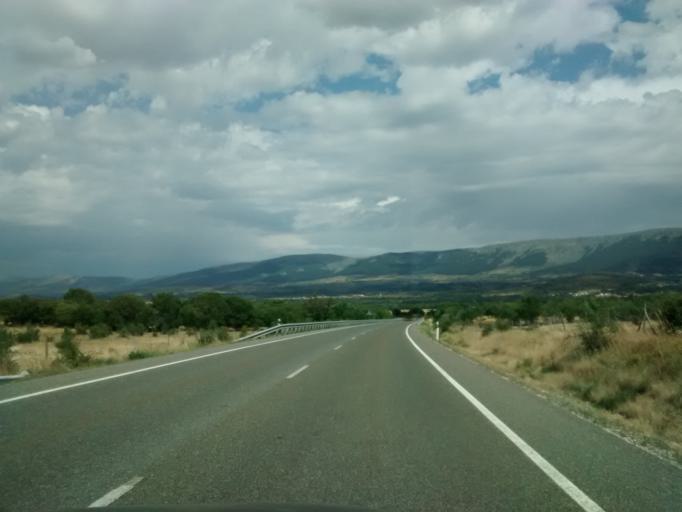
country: ES
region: Castille and Leon
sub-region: Provincia de Segovia
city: Navafria
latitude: 41.0644
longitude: -3.8477
